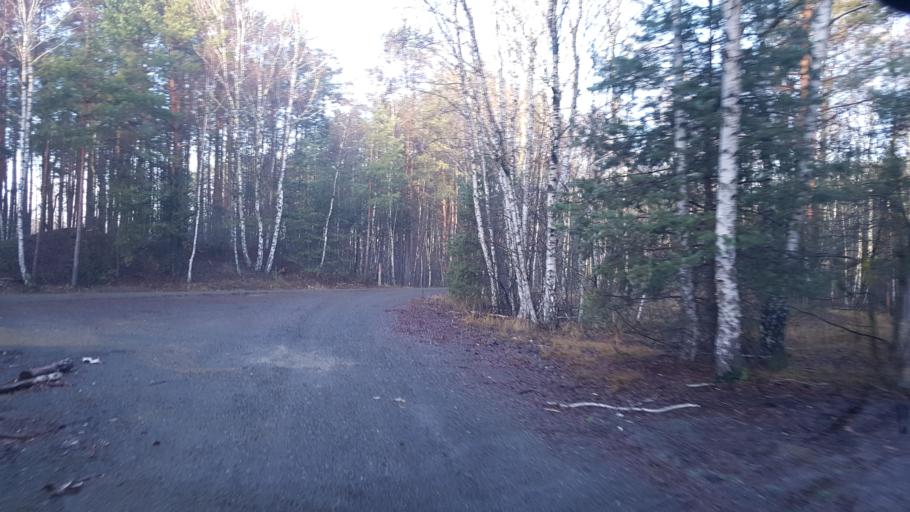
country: DE
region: Brandenburg
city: Trobitz
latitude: 51.5795
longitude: 13.4577
